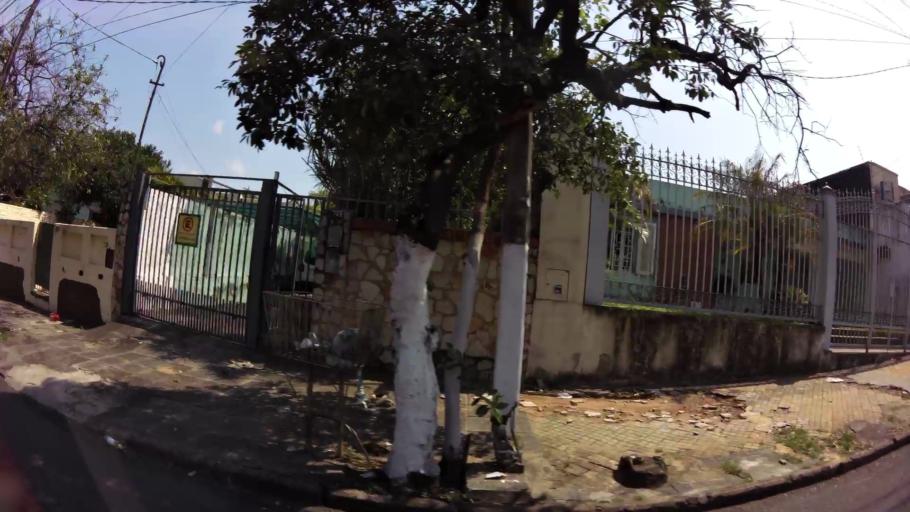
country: PY
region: Presidente Hayes
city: Nanawa
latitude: -25.2843
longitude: -57.6524
